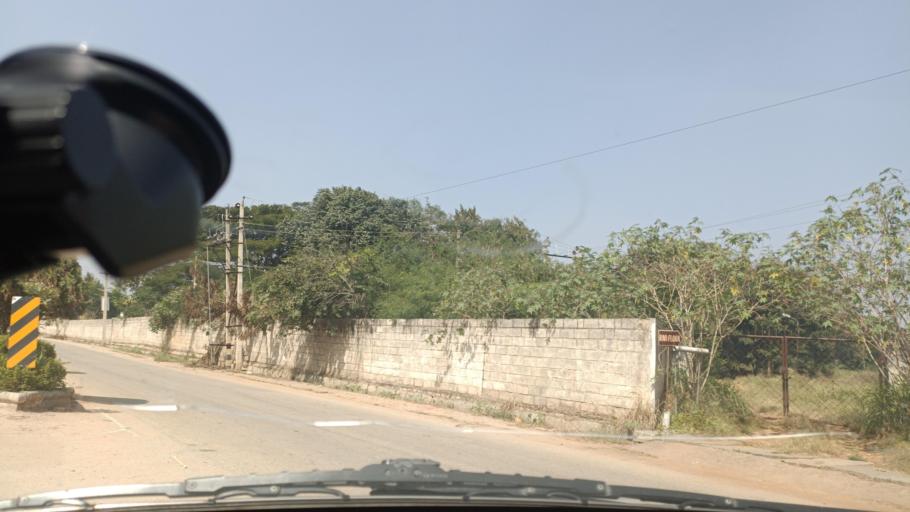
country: IN
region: Karnataka
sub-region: Bangalore Rural
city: Devanhalli
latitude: 13.1973
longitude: 77.6422
